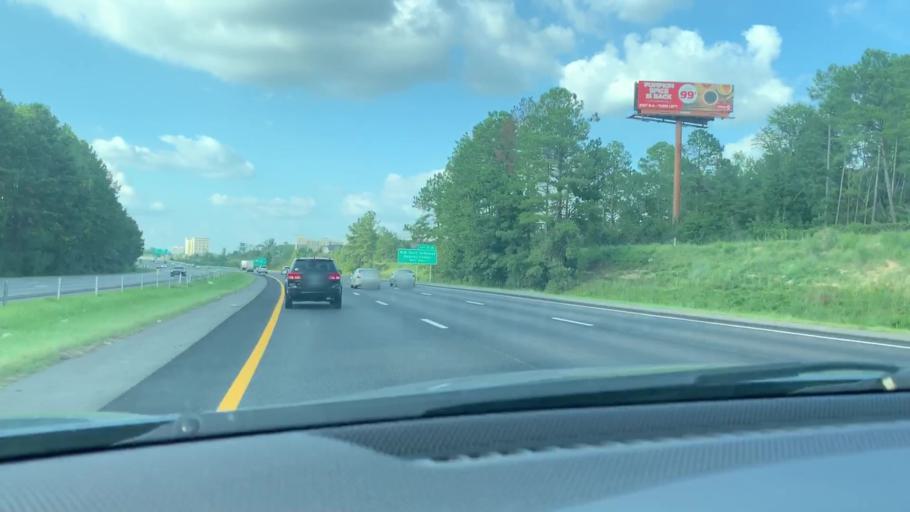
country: US
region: South Carolina
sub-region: Richland County
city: Forest Acres
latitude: 33.9627
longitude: -80.9529
